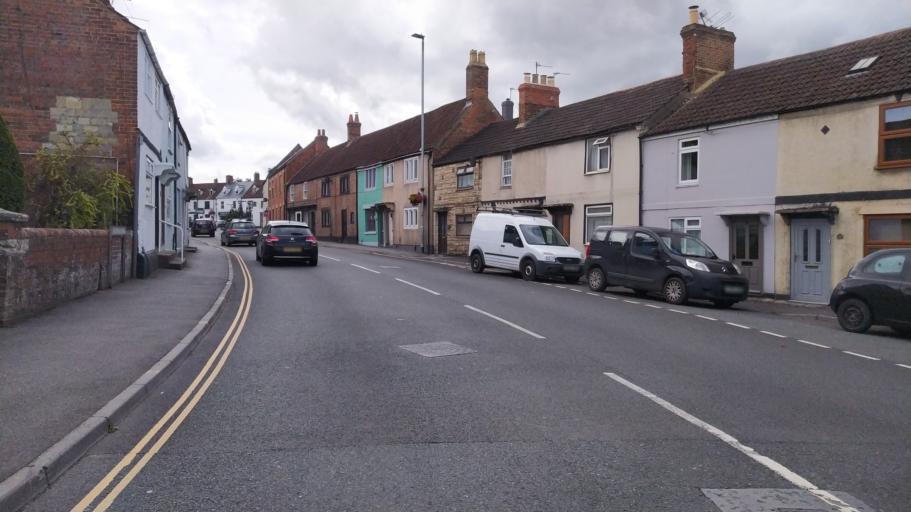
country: GB
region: England
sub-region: Wiltshire
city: Westbury
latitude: 51.2640
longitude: -2.1823
